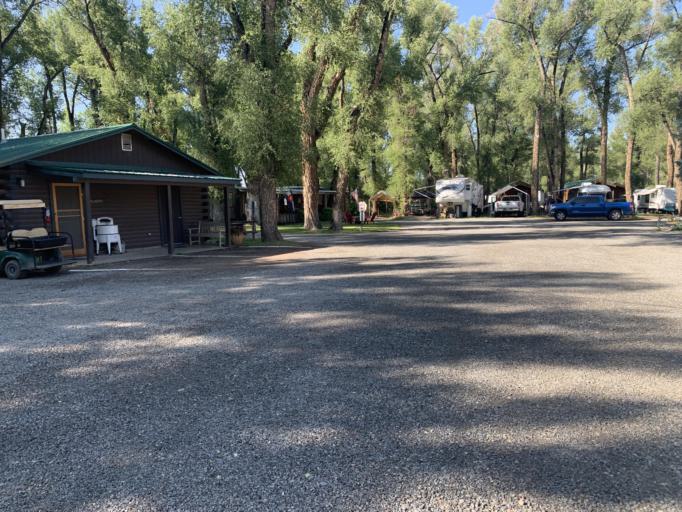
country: US
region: Colorado
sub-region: Gunnison County
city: Gunnison
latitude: 38.5813
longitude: -106.9185
